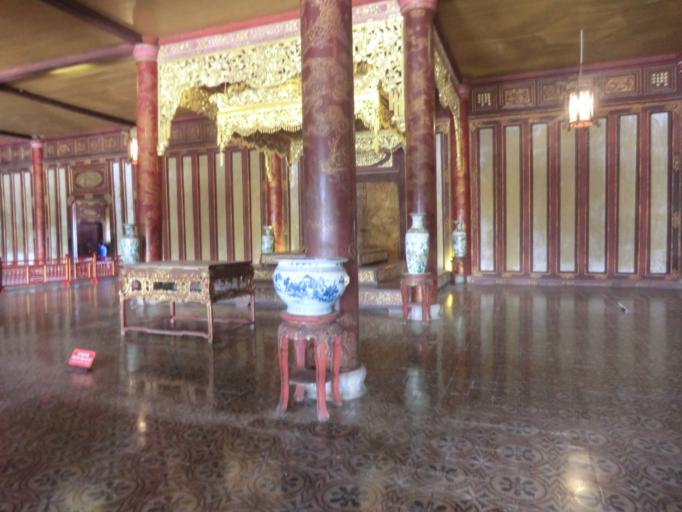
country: VN
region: Thua Thien-Hue
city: Hue
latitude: 16.4685
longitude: 107.5782
